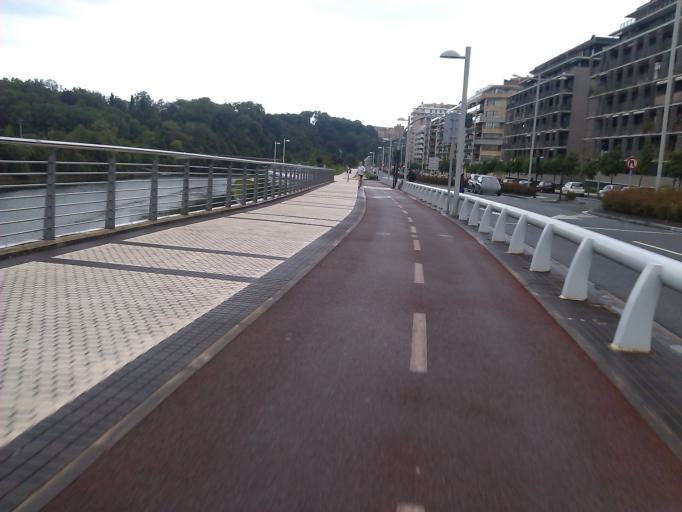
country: ES
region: Basque Country
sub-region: Provincia de Guipuzcoa
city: San Sebastian
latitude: 43.3085
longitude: -1.9733
